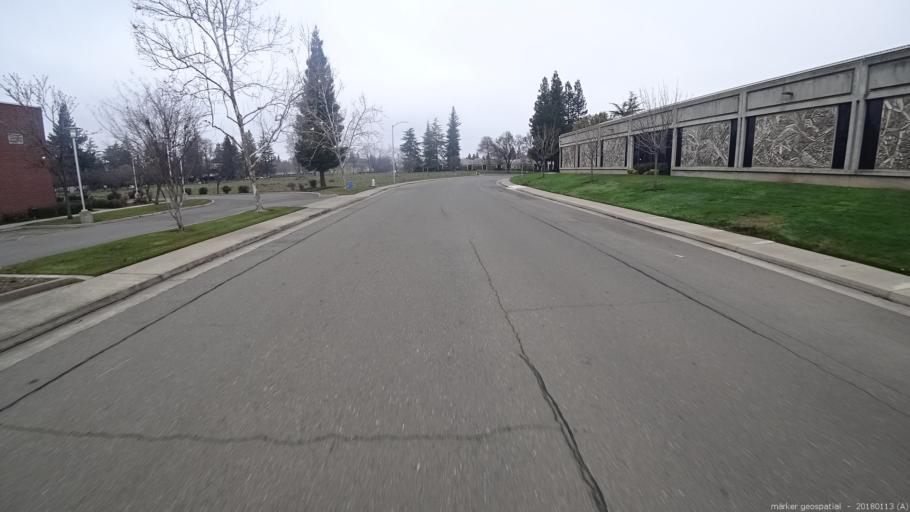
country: US
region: California
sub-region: Sacramento County
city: Rancho Cordova
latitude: 38.5941
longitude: -121.2729
